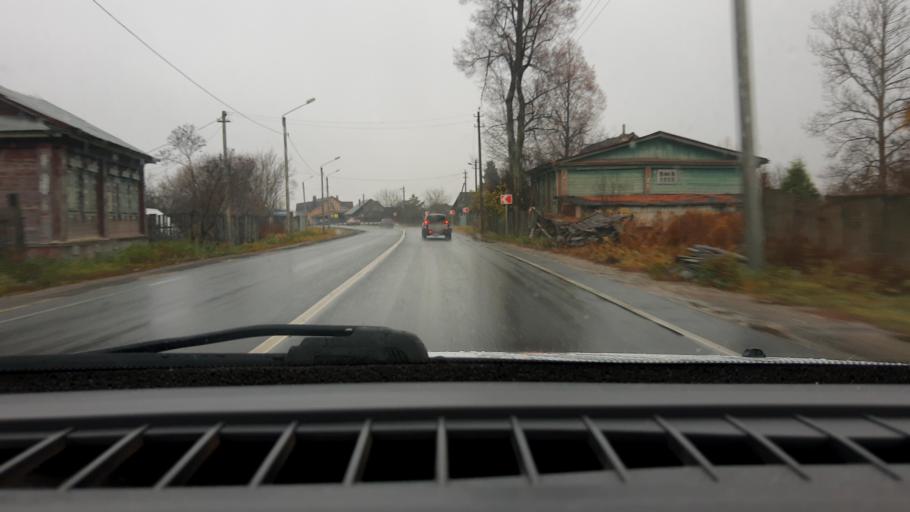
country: RU
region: Nizjnij Novgorod
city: Sitniki
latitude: 56.5455
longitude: 44.0192
